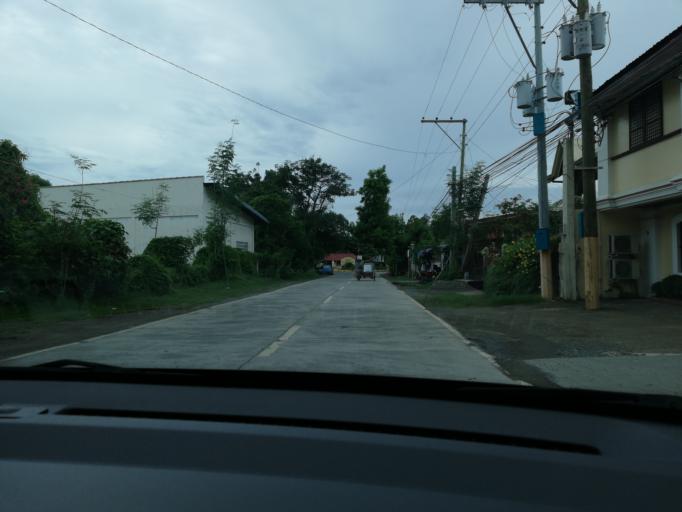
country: PH
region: Ilocos
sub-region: Province of Ilocos Sur
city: Bantay
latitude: 17.5847
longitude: 120.3814
